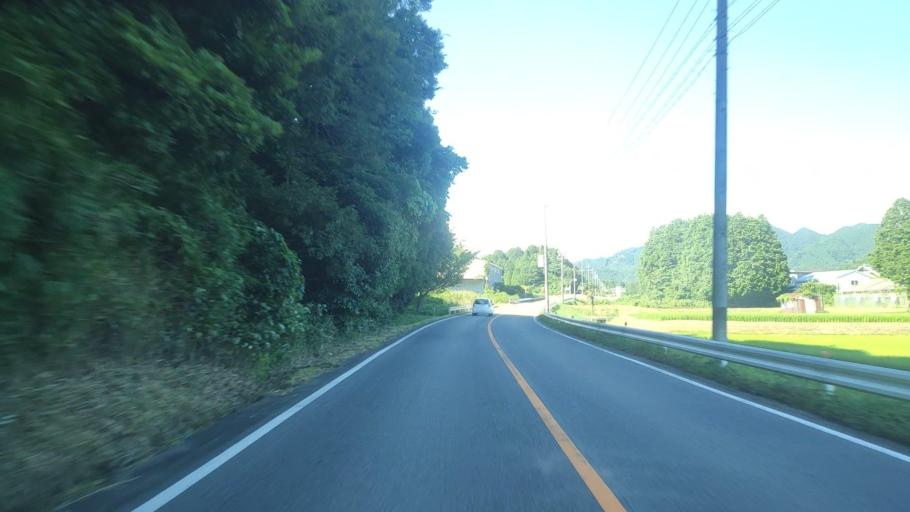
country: JP
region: Shiga Prefecture
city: Minakuchicho-matoba
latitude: 34.8500
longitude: 136.2427
